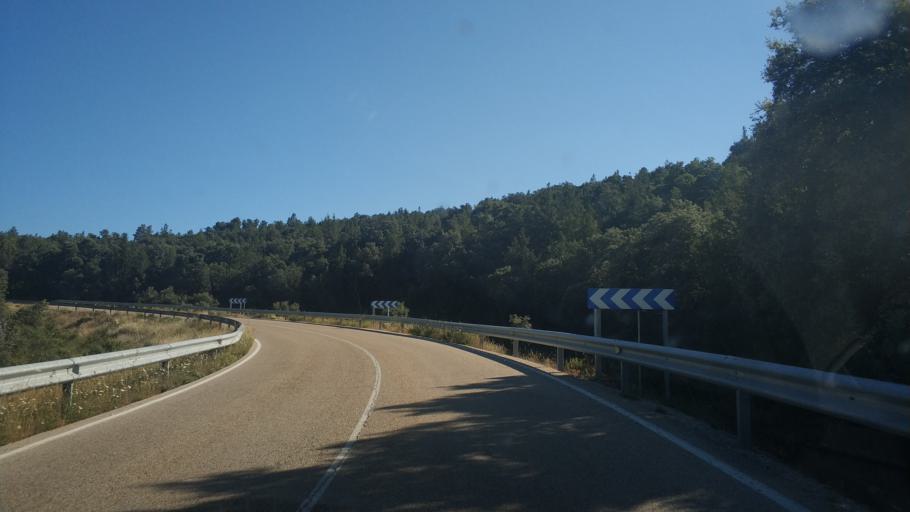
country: ES
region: Castille and Leon
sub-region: Provincia de Soria
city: Montejo de Tiermes
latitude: 41.4223
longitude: -3.2050
